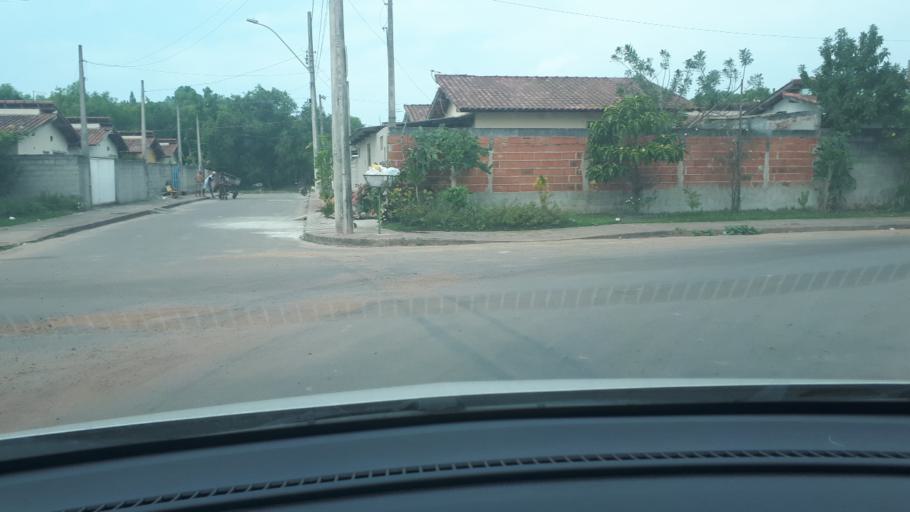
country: BR
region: Espirito Santo
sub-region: Serra
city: Serra
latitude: -20.1447
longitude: -40.1921
